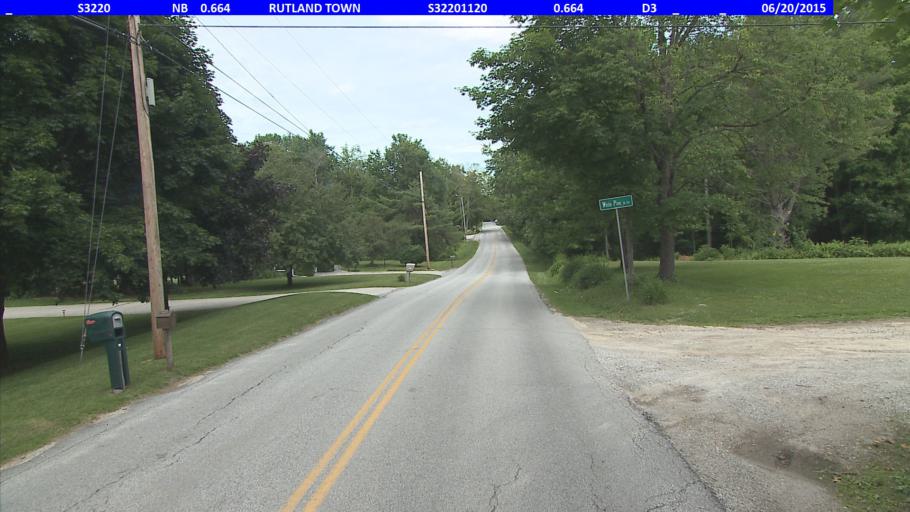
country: US
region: Vermont
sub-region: Rutland County
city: Rutland
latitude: 43.6183
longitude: -72.9365
